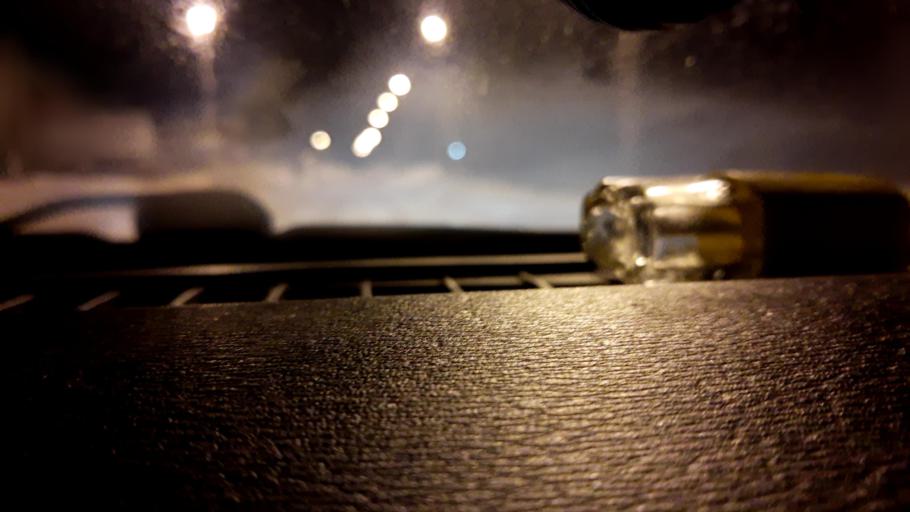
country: RU
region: Bashkortostan
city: Kabakovo
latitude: 54.6180
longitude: 56.0683
